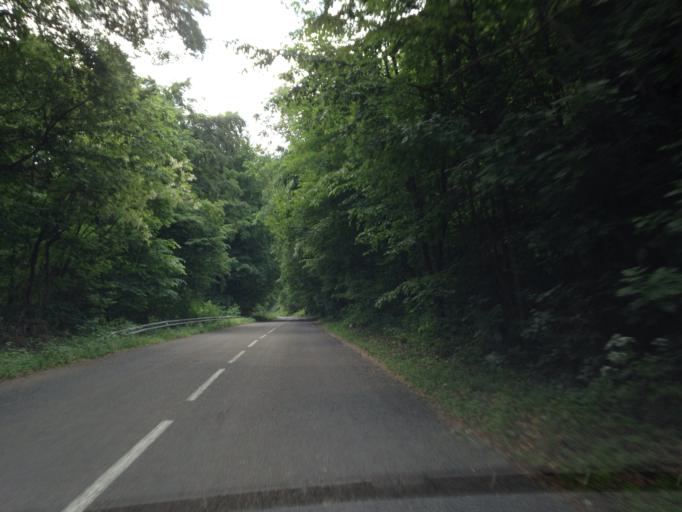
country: HU
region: Pest
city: Visegrad
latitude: 47.7441
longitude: 18.9435
